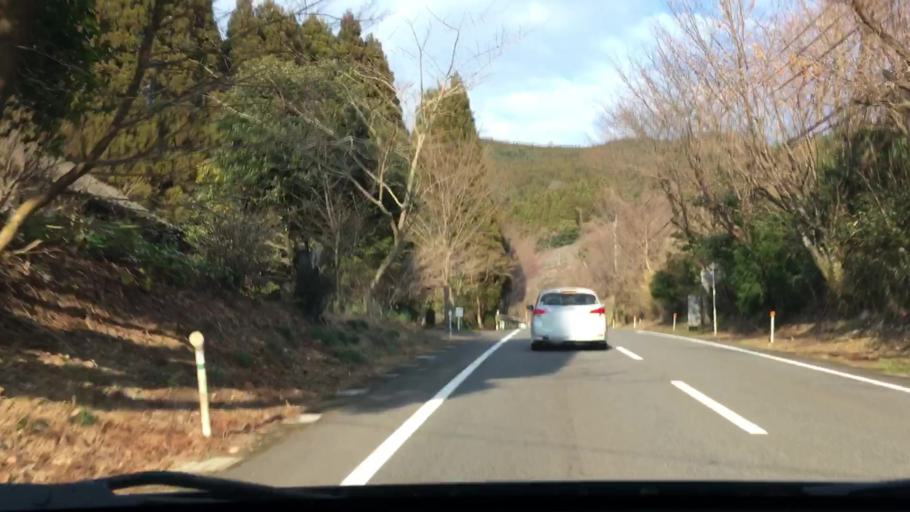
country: JP
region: Miyazaki
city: Miyazaki-shi
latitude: 31.7742
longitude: 131.3316
